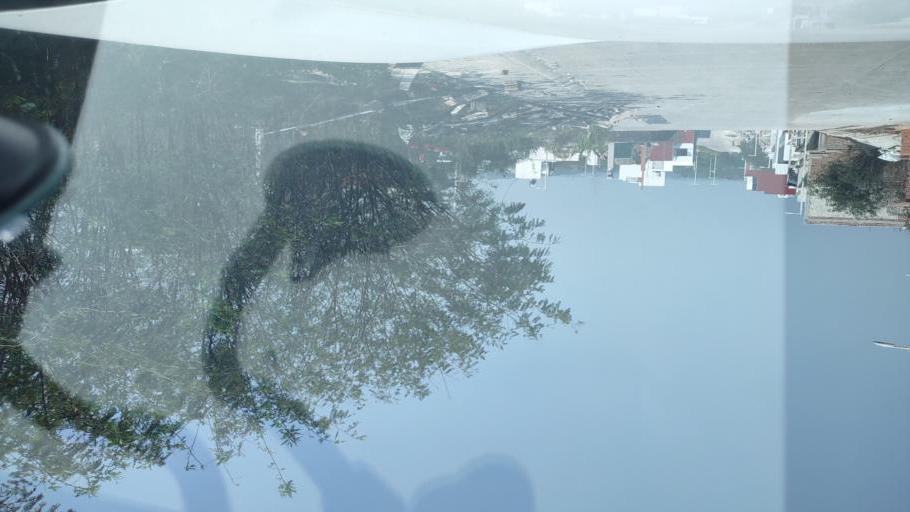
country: MX
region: Veracruz
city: El Castillo
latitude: 19.5295
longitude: -96.8718
